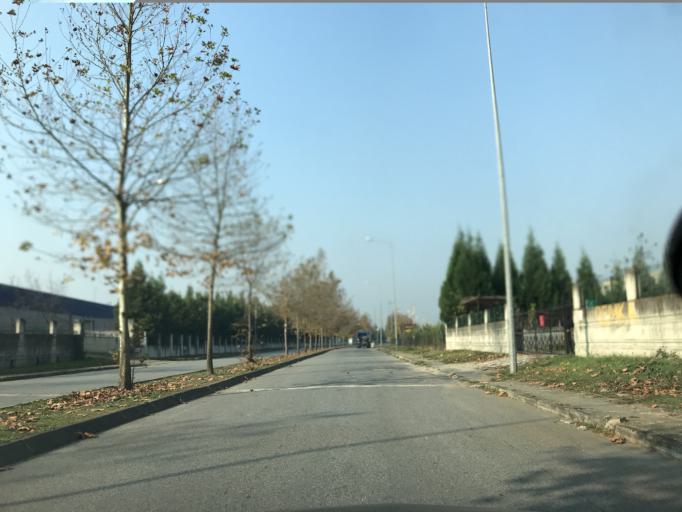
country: TR
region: Duzce
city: Duzce
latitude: 40.7871
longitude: 31.1386
